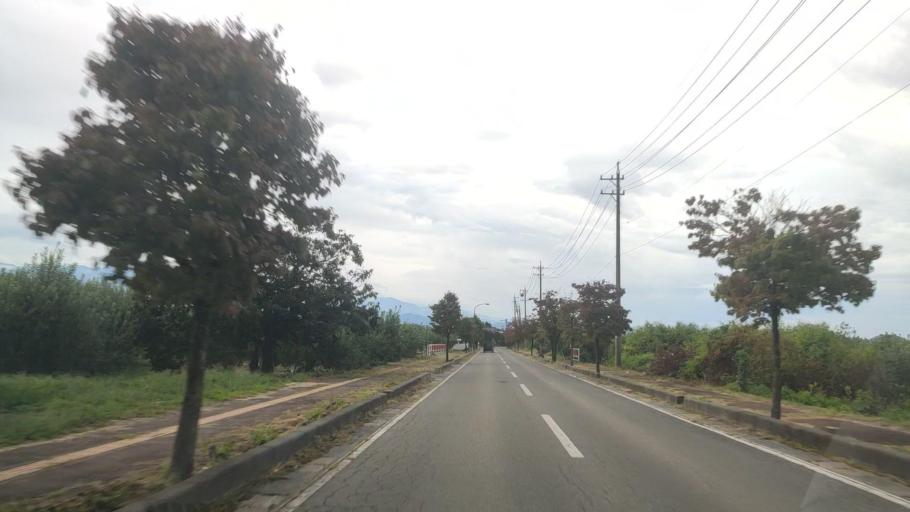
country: JP
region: Nagano
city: Nakano
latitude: 36.7849
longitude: 138.3561
